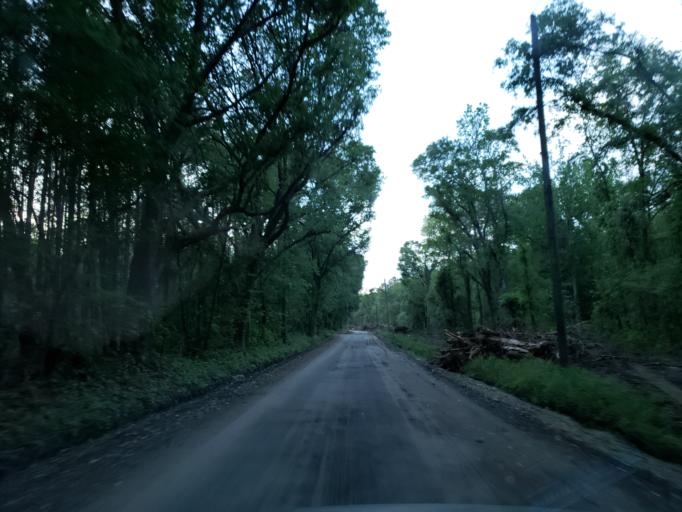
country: US
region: Georgia
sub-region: Lowndes County
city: Hahira
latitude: 30.9525
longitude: -83.3904
